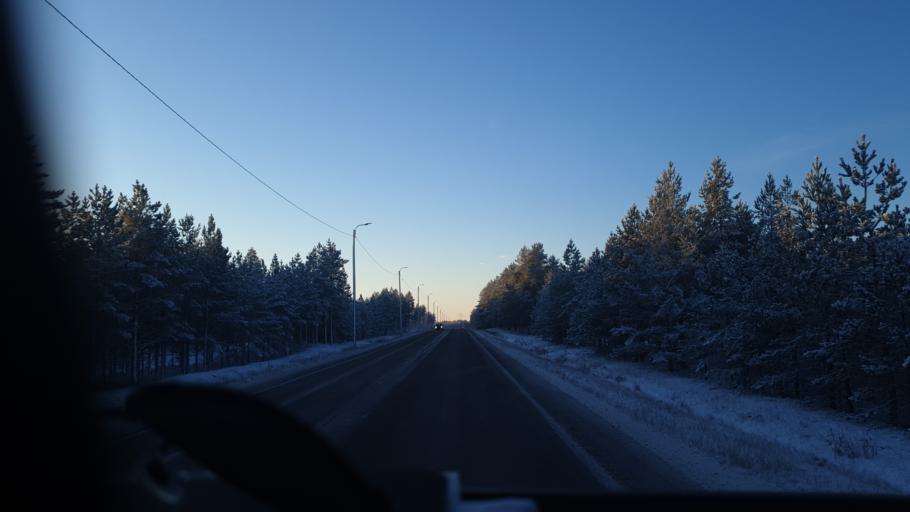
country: FI
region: Northern Ostrobothnia
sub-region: Ylivieska
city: Kalajoki
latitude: 64.2362
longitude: 23.8313
